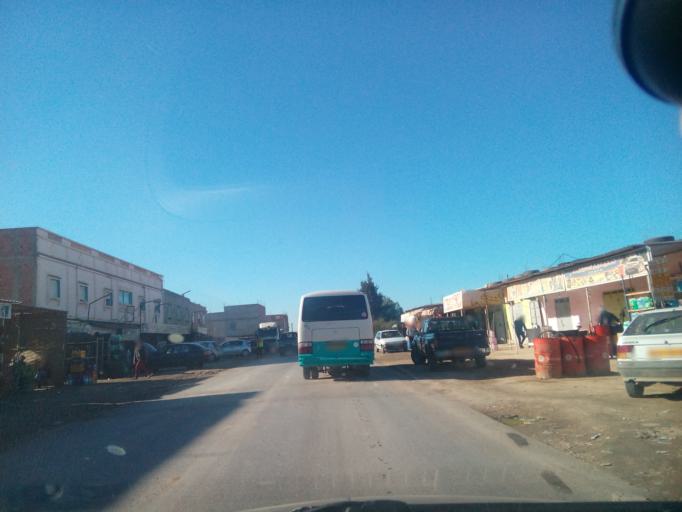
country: DZ
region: Relizane
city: Djidiouia
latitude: 35.8960
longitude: 0.6943
